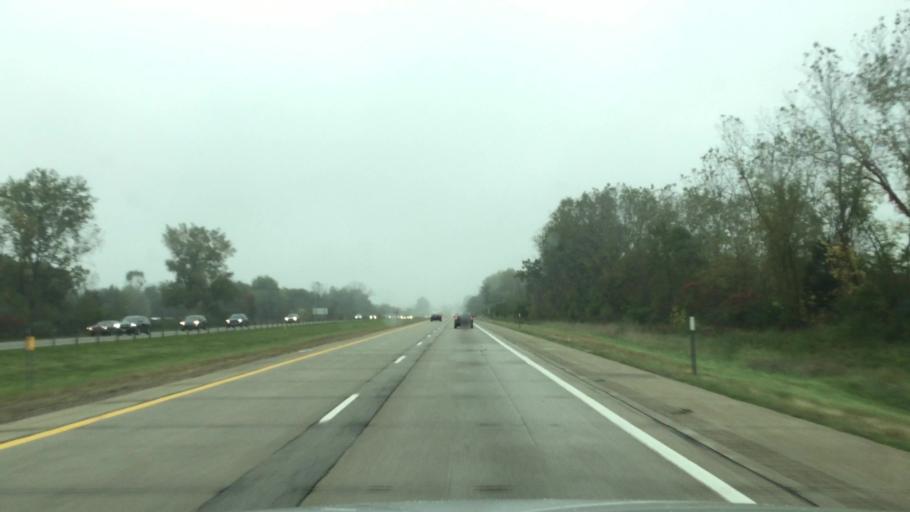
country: US
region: Michigan
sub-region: Van Buren County
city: Hartford
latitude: 42.1936
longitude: -86.1420
